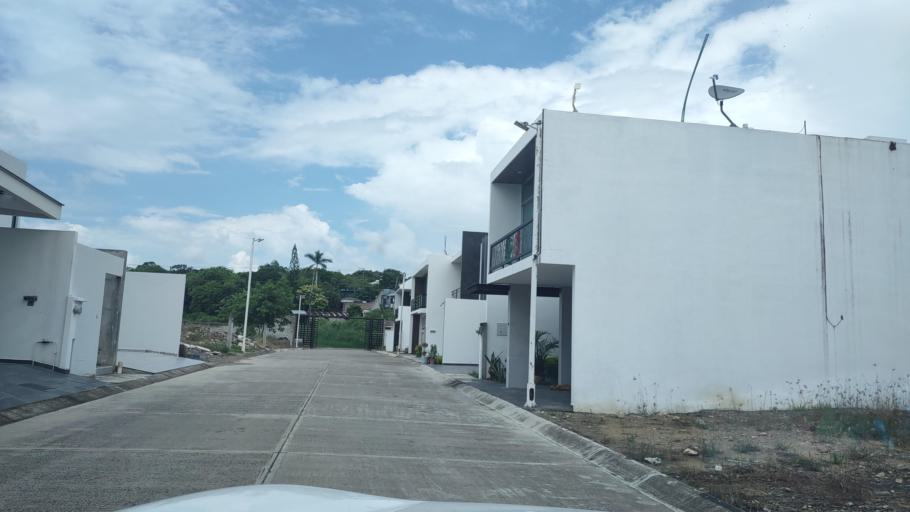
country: MX
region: Veracruz
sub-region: Tuxpan
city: Alto Lucero
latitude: 20.9461
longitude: -97.4295
